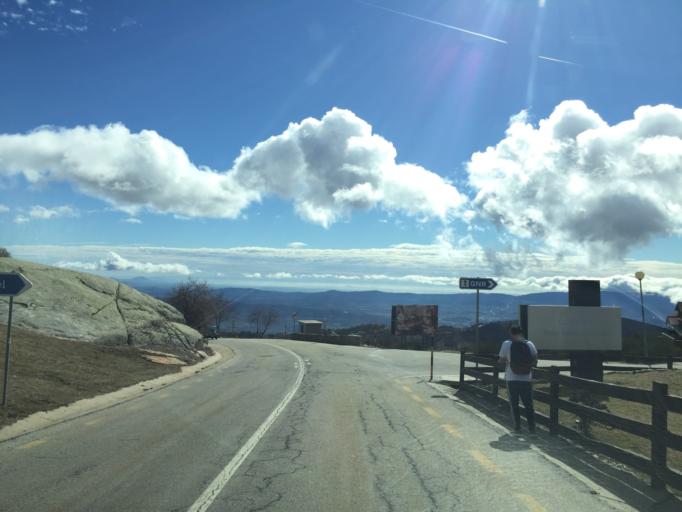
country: PT
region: Castelo Branco
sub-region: Covilha
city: Covilha
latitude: 40.3075
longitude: -7.5484
